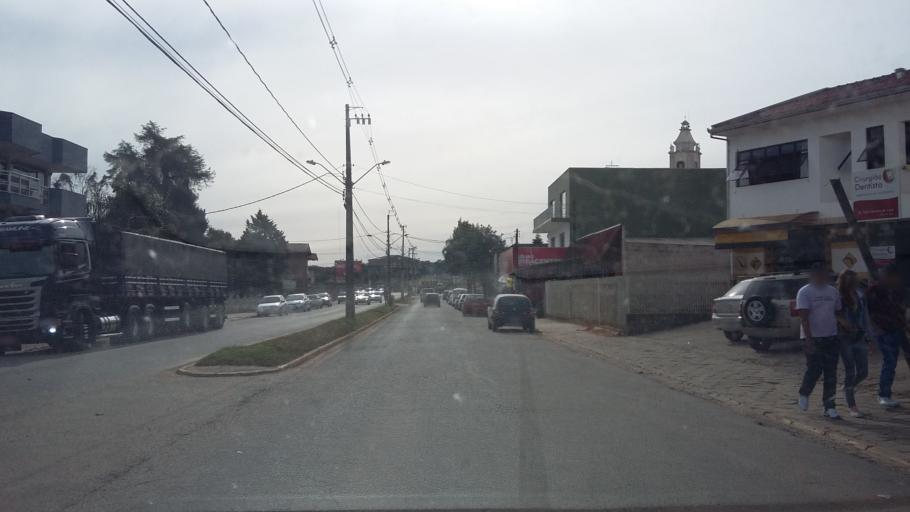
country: BR
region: Parana
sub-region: Lapa
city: Lapa
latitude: -25.8738
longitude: -49.4998
